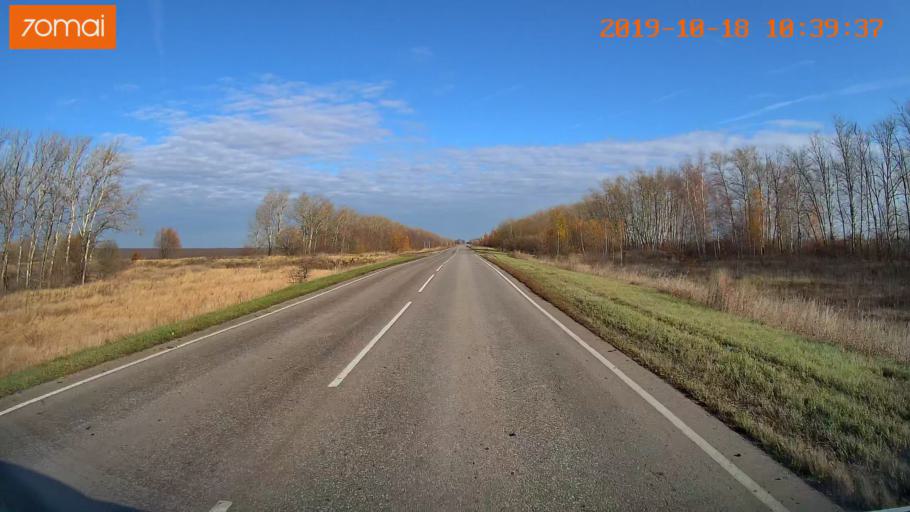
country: RU
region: Tula
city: Kurkino
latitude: 53.5895
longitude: 38.6550
